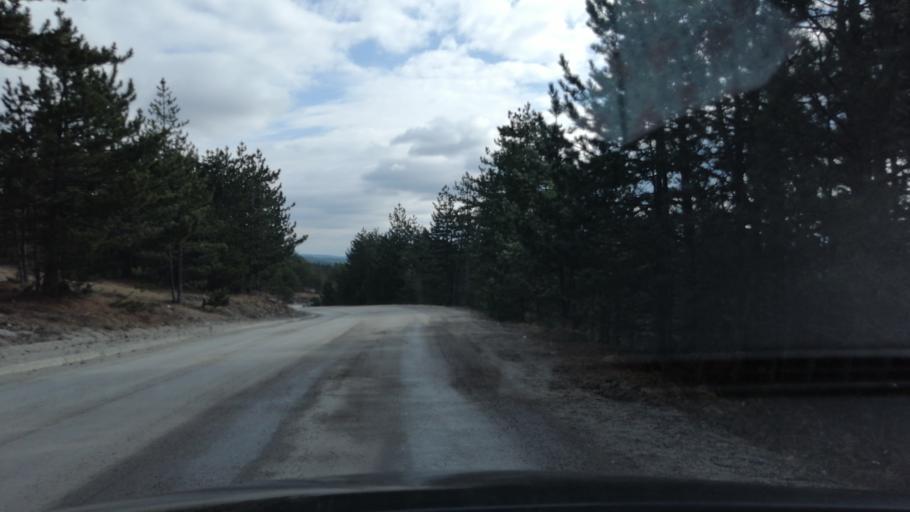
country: RS
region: Central Serbia
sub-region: Zlatiborski Okrug
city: Bajina Basta
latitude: 43.8781
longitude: 19.5578
